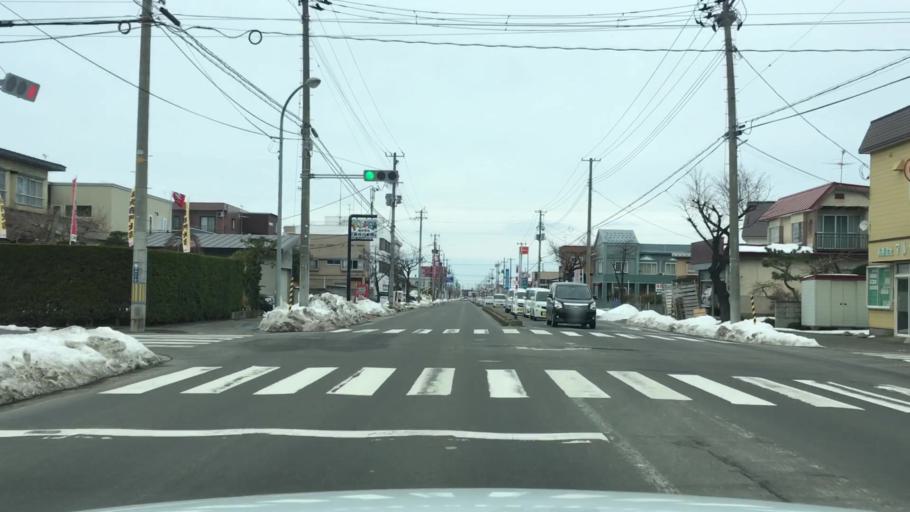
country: JP
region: Aomori
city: Hirosaki
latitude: 40.5967
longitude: 140.4924
